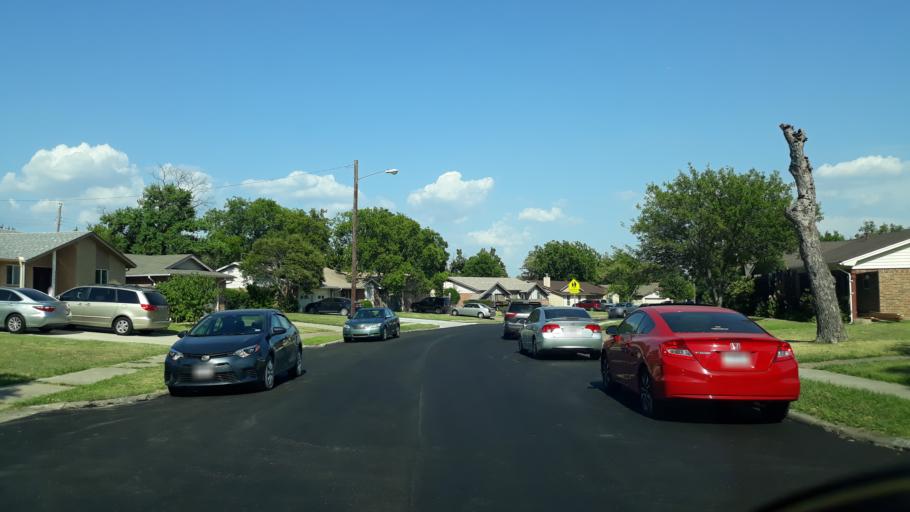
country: US
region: Texas
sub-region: Dallas County
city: Irving
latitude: 32.8448
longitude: -97.0055
